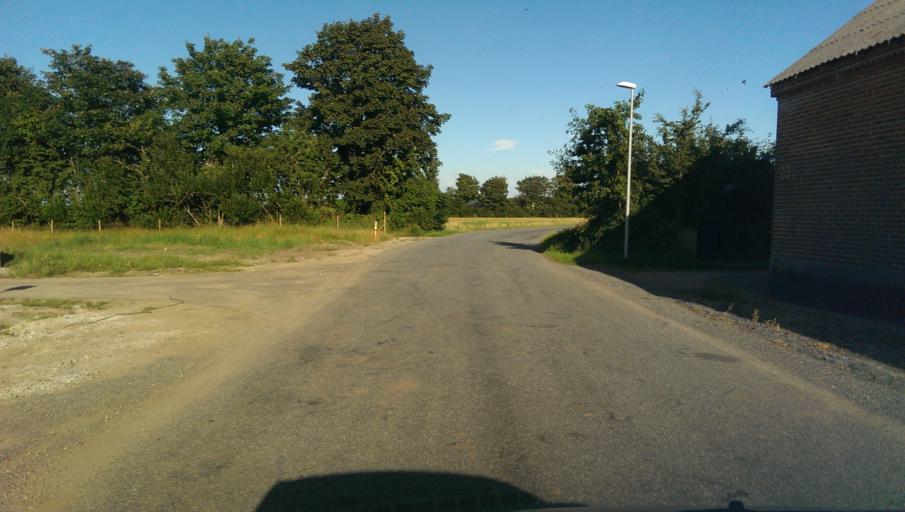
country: DK
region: South Denmark
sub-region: Esbjerg Kommune
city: Esbjerg
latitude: 55.5328
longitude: 8.4825
